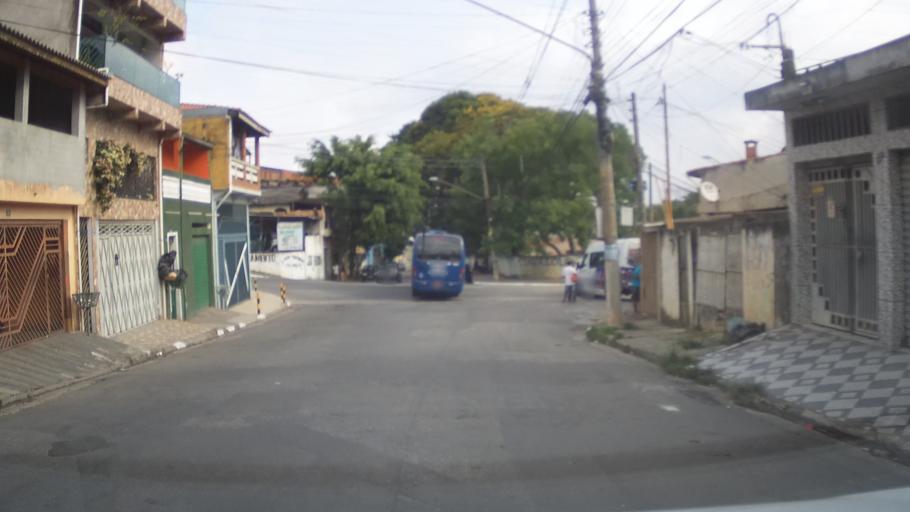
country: BR
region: Sao Paulo
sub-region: Guarulhos
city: Guarulhos
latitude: -23.4142
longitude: -46.5095
